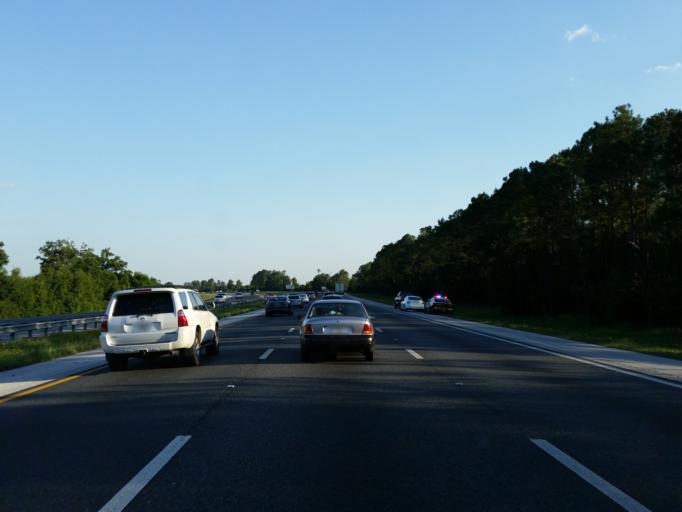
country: US
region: Florida
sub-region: Marion County
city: Ocala
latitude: 29.0833
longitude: -82.1852
